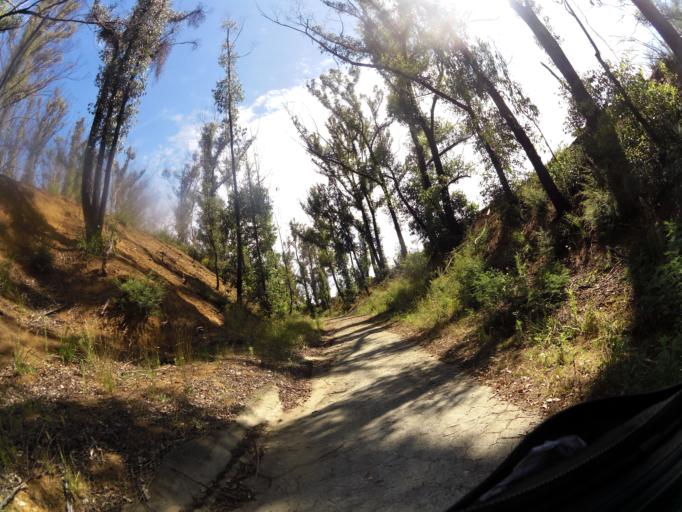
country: AU
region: Victoria
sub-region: East Gippsland
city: Lakes Entrance
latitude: -37.7307
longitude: 148.1626
